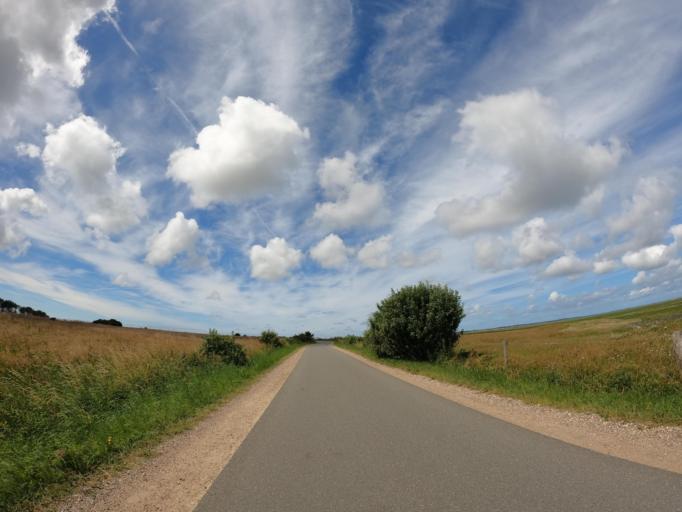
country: DE
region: Schleswig-Holstein
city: Sylt-Ost
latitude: 54.8761
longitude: 8.4145
